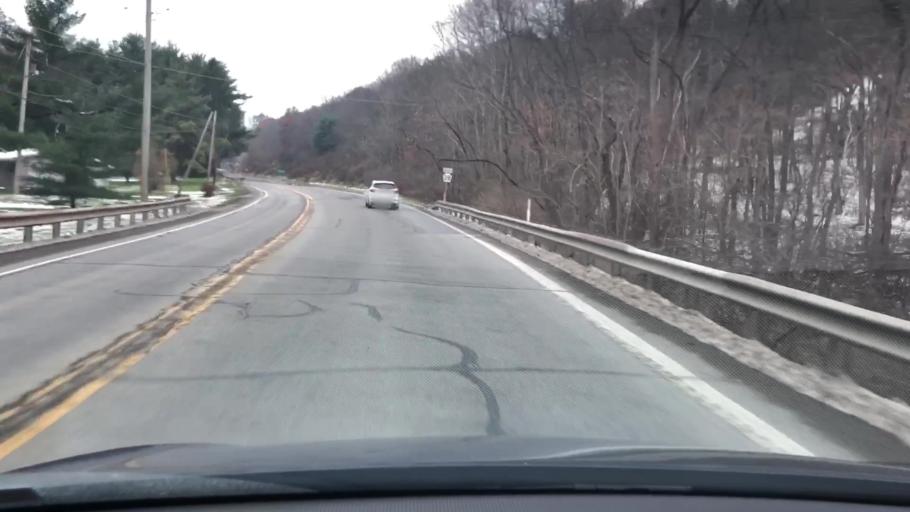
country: US
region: Pennsylvania
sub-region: Jefferson County
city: Brookville
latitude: 41.1177
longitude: -79.1969
